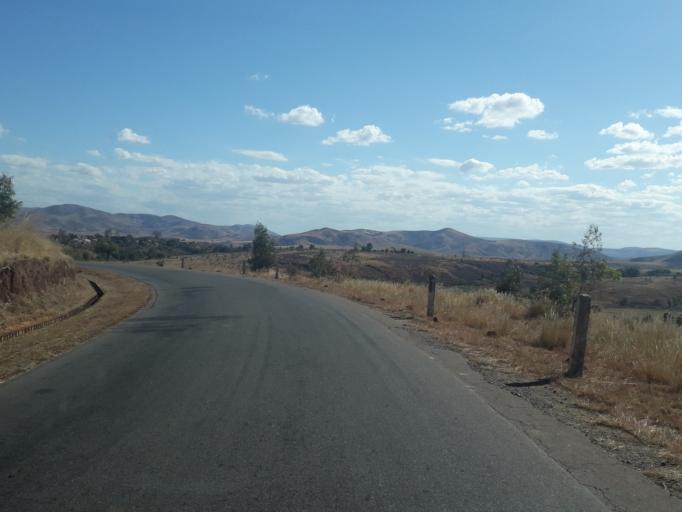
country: MG
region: Betsiboka
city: Maevatanana
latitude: -17.5878
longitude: 46.9373
